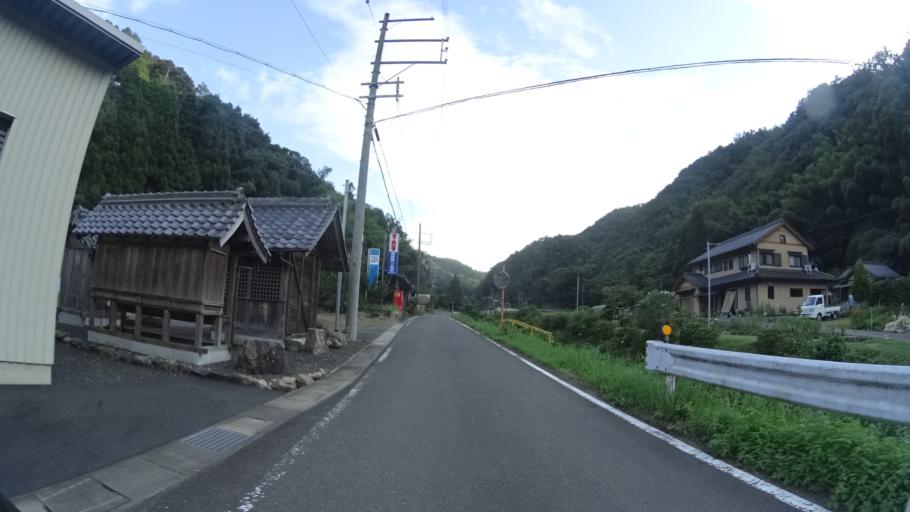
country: JP
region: Kyoto
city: Maizuru
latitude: 35.4046
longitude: 135.3501
